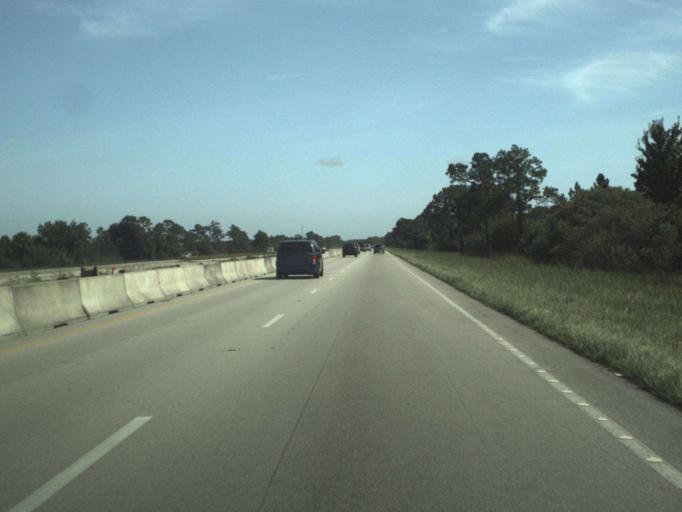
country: US
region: Florida
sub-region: Indian River County
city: Fellsmere
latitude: 27.7930
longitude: -80.5494
